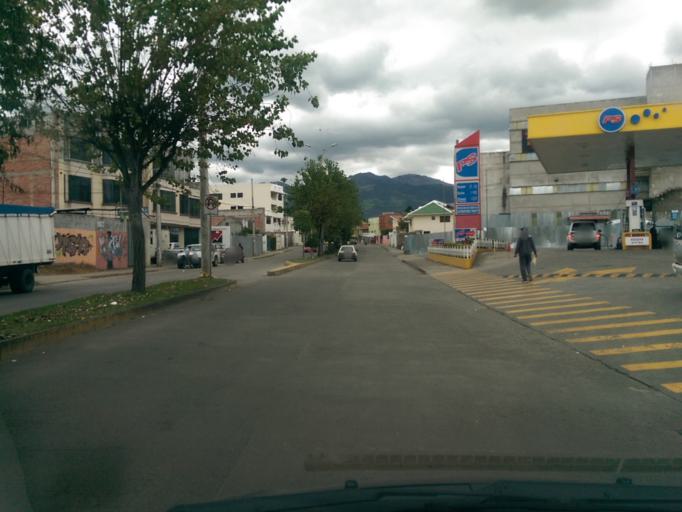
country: EC
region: Azuay
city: Cuenca
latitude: -2.9103
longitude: -79.0226
